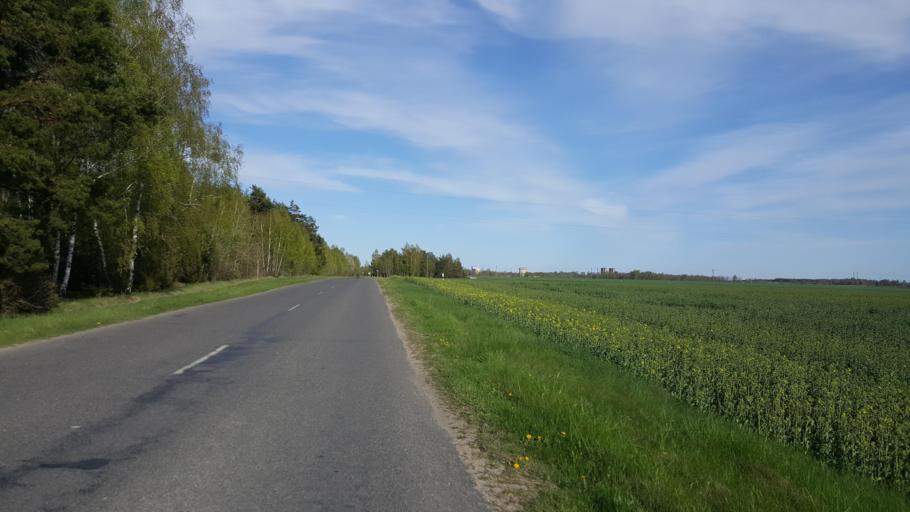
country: BY
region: Brest
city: Vysokaye
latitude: 52.4010
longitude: 23.4724
